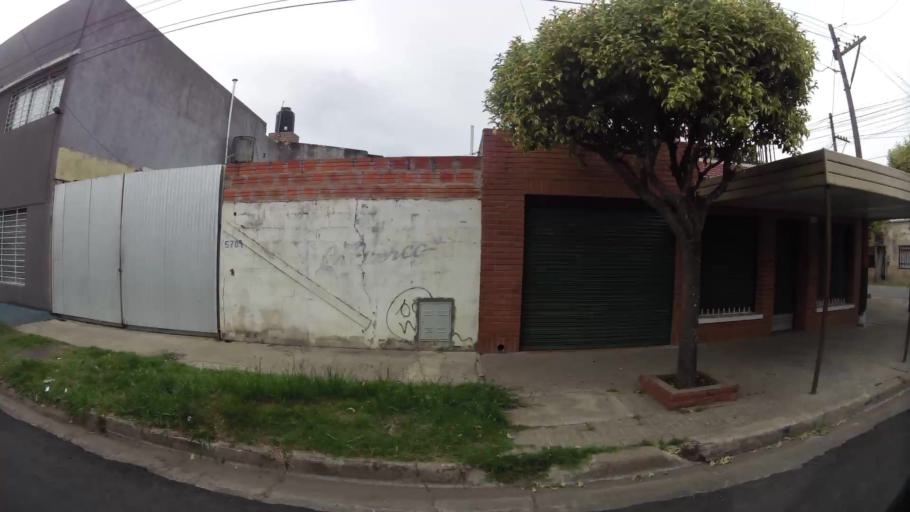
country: AR
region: Santa Fe
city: Gobernador Galvez
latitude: -33.0043
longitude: -60.6604
